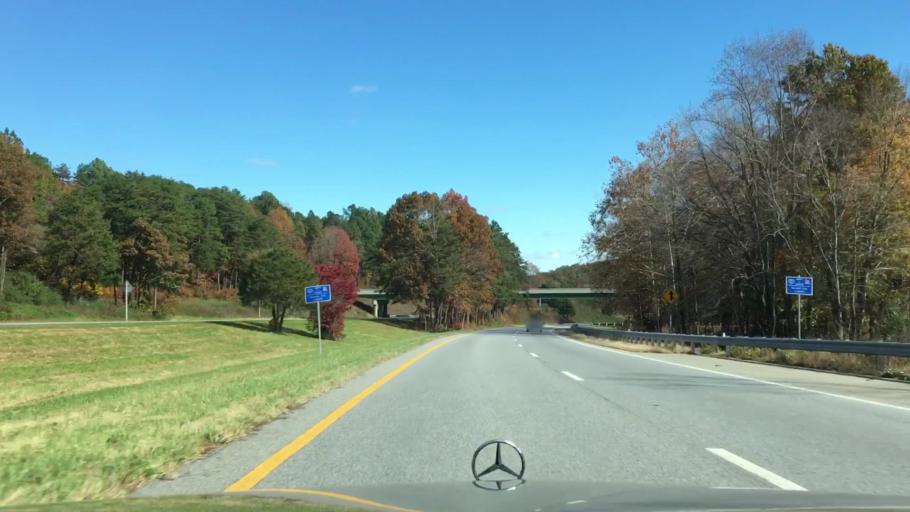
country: US
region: Virginia
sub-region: Campbell County
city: Altavista
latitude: 37.1350
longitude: -79.2928
